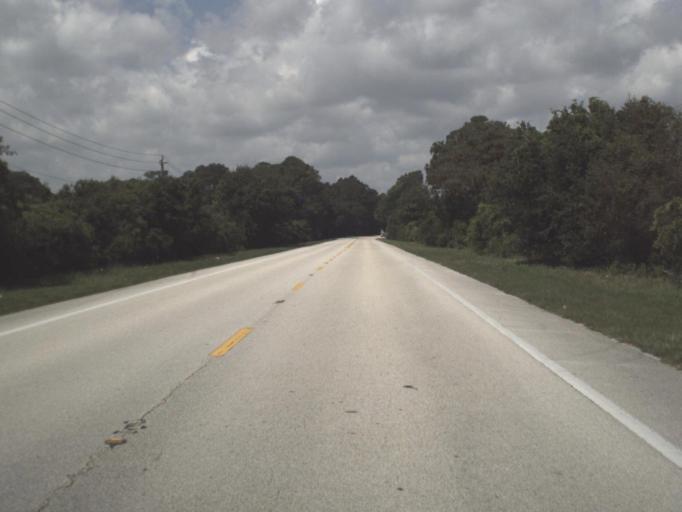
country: US
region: Florida
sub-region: Saint Johns County
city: Butler Beach
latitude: 29.7597
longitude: -81.2693
